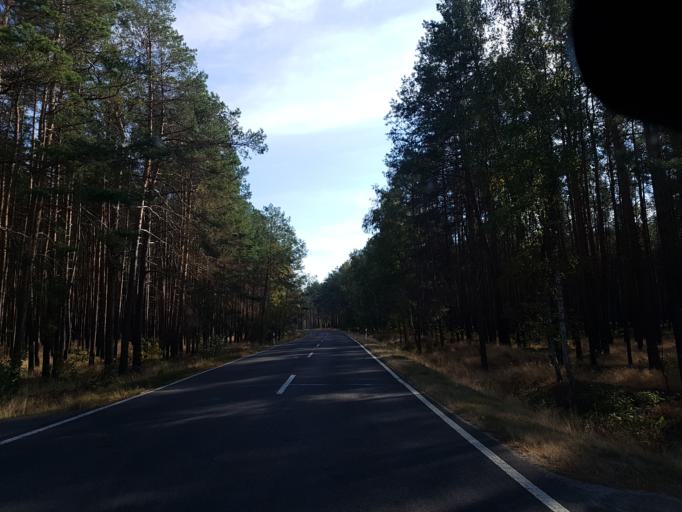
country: DE
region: Brandenburg
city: Schonborn
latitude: 51.6798
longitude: 13.4643
